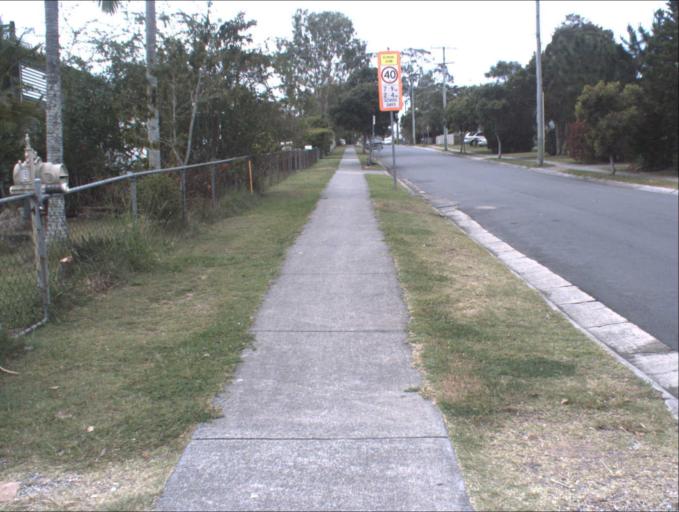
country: AU
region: Queensland
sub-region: Logan
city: Logan City
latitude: -27.6321
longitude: 153.1138
